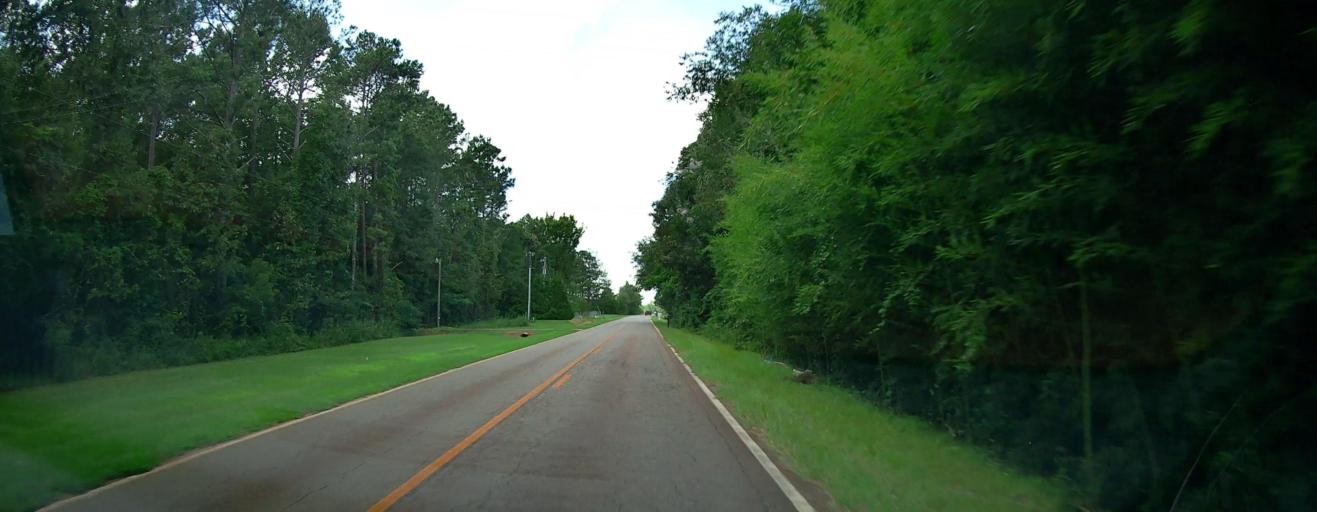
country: US
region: Georgia
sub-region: Houston County
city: Perry
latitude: 32.5221
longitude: -83.7567
